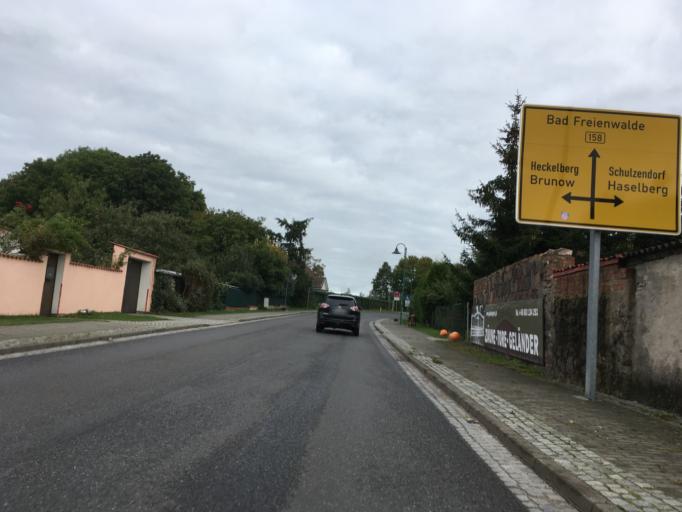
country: DE
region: Brandenburg
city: Protzel
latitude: 52.7087
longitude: 13.9229
